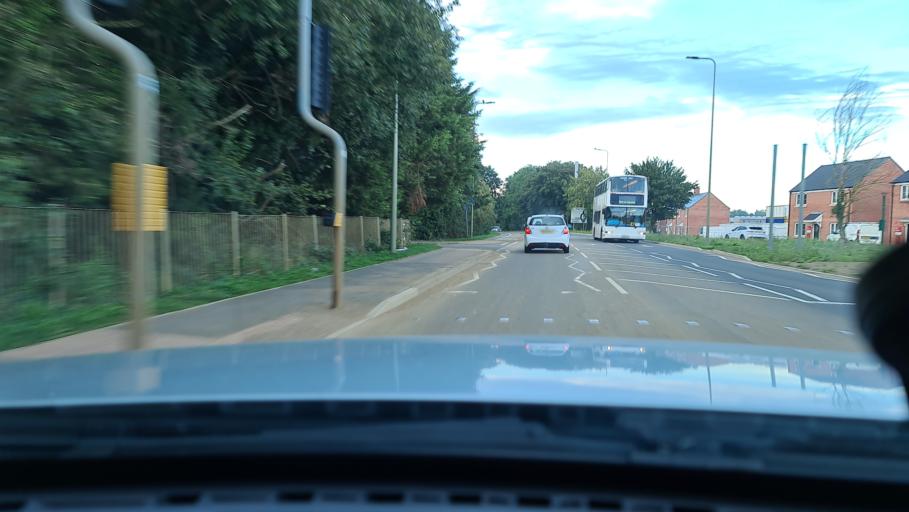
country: GB
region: England
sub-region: Oxfordshire
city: Hanwell
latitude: 52.0768
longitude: -1.3667
